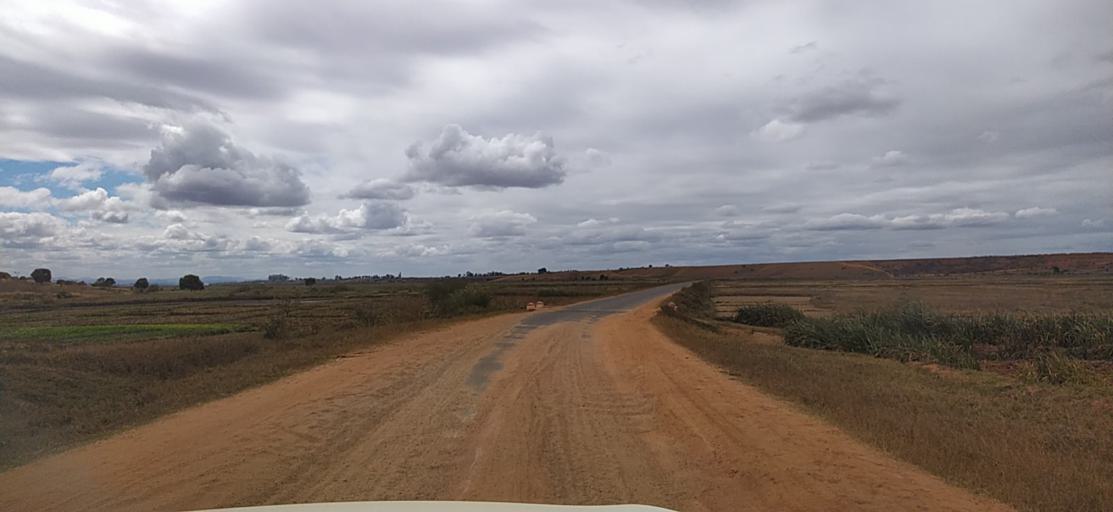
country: MG
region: Alaotra Mangoro
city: Ambatondrazaka
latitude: -17.9215
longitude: 48.2576
